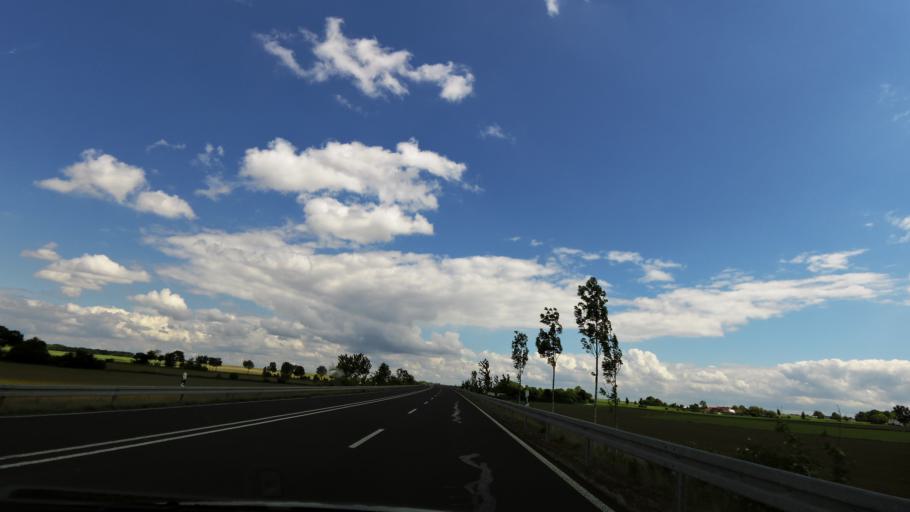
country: DE
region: North Rhine-Westphalia
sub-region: Regierungsbezirk Koln
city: Selfkant
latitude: 51.0131
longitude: 5.9593
